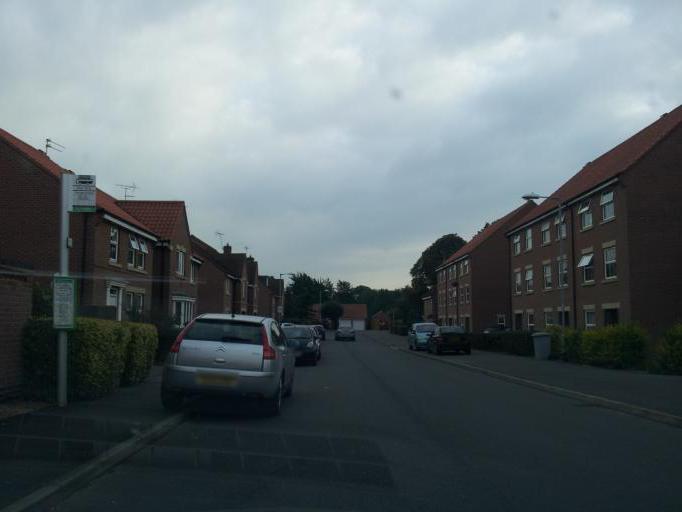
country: GB
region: England
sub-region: Nottinghamshire
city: Newark on Trent
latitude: 53.0471
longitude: -0.7729
